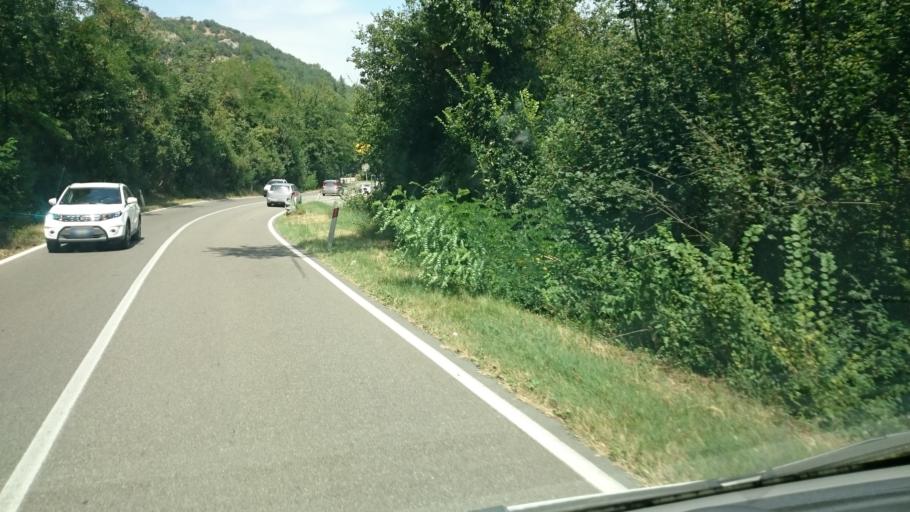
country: IT
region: Emilia-Romagna
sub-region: Provincia di Reggio Emilia
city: Vezzano sul Crostolo
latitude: 44.5872
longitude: 10.5352
